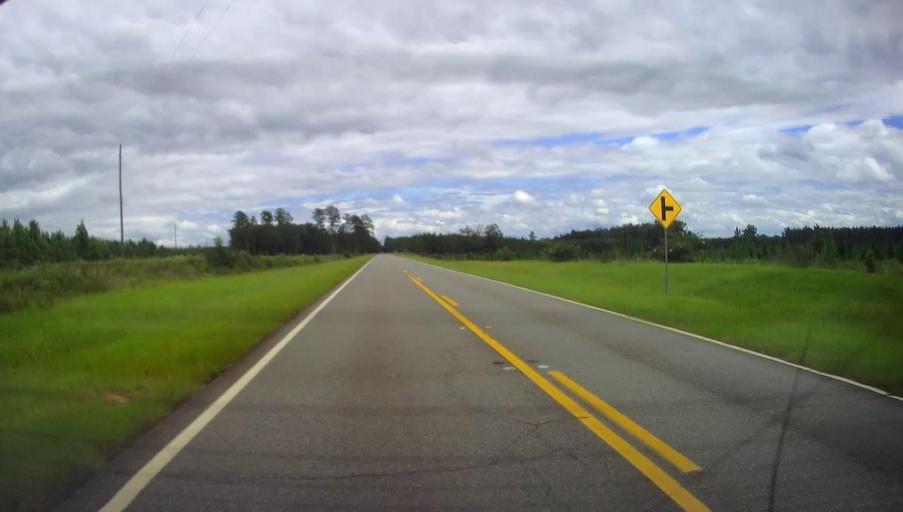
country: US
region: Georgia
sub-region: Twiggs County
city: Jeffersonville
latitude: 32.6804
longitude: -83.3091
